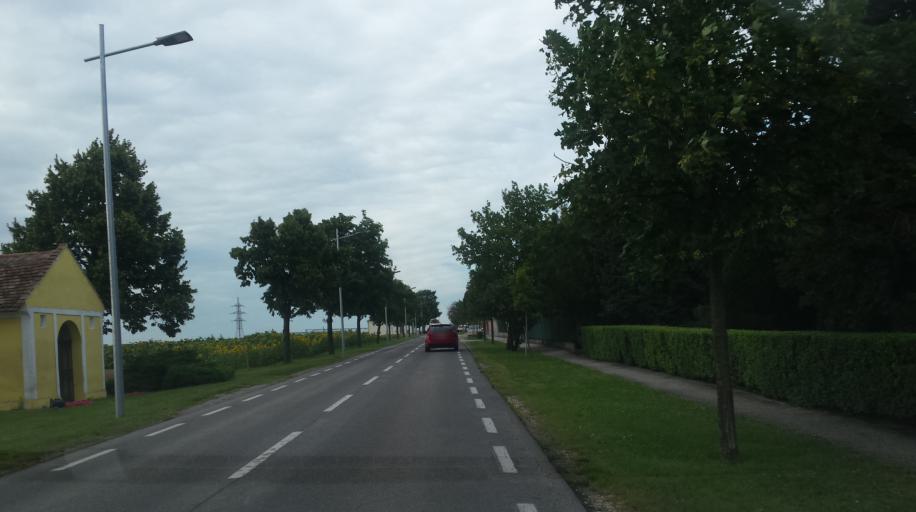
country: AT
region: Lower Austria
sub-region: Politischer Bezirk Wien-Umgebung
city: Moosbrunn
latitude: 48.0234
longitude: 16.4624
